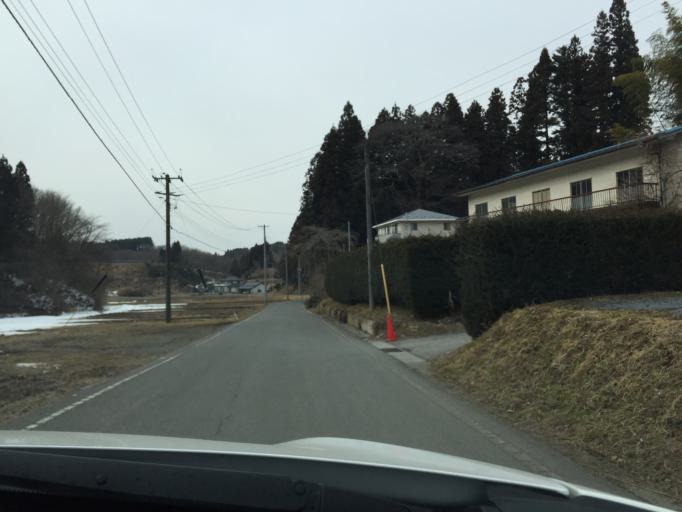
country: JP
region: Fukushima
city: Ishikawa
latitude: 37.1759
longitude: 140.5726
